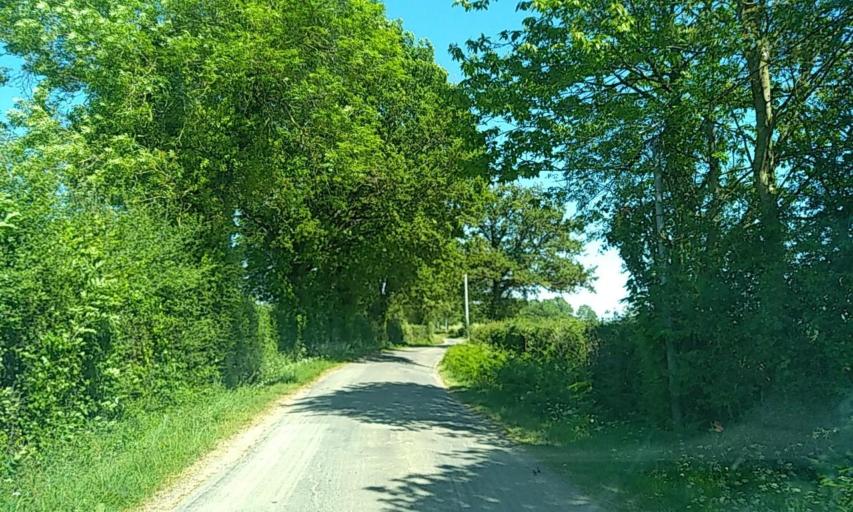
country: FR
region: Poitou-Charentes
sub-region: Departement des Deux-Sevres
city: La Chapelle-Saint-Laurent
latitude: 46.7816
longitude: -0.4745
